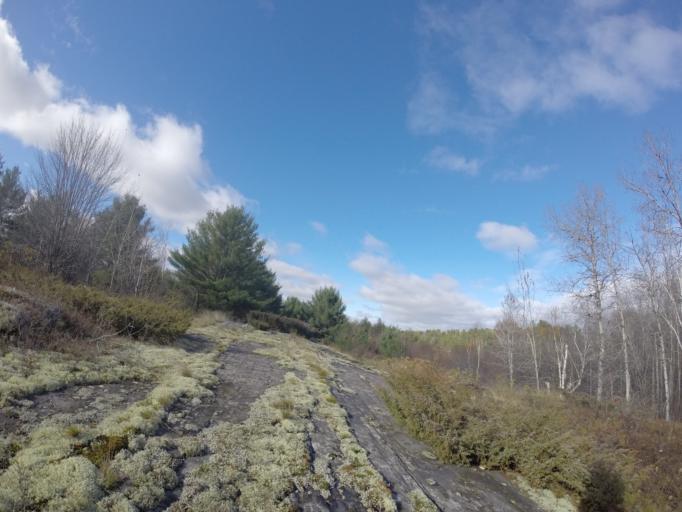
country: CA
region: Ontario
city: Greater Sudbury
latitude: 46.1086
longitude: -80.6512
